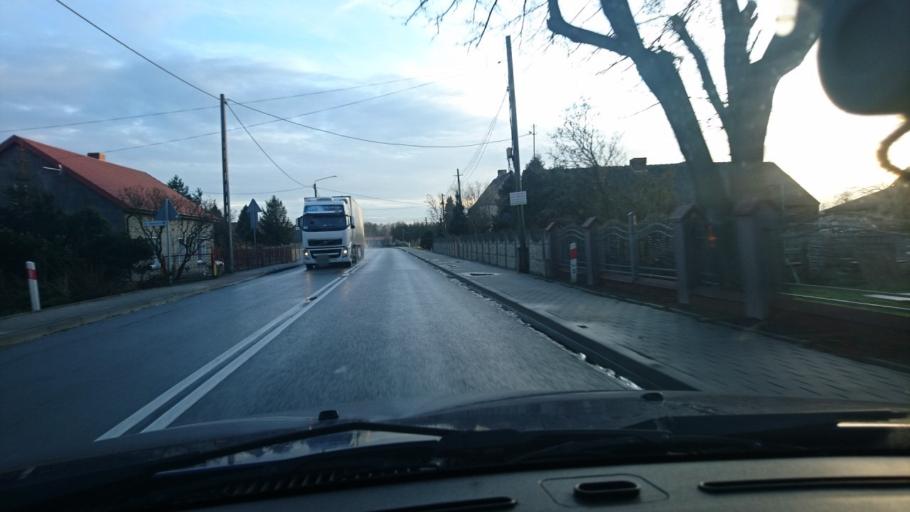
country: PL
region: Greater Poland Voivodeship
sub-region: Powiat kepinski
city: Opatow
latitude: 51.1695
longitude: 18.1466
